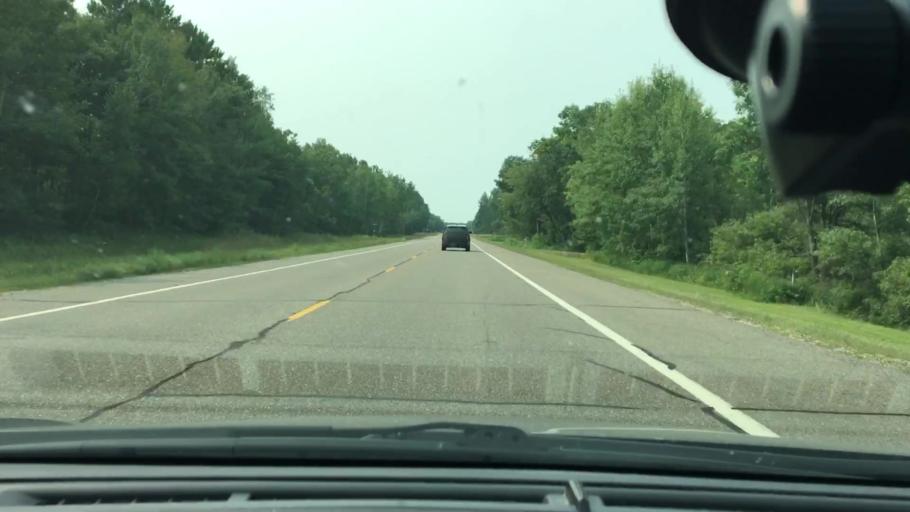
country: US
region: Minnesota
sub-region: Crow Wing County
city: Breezy Point
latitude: 46.5078
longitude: -94.1373
